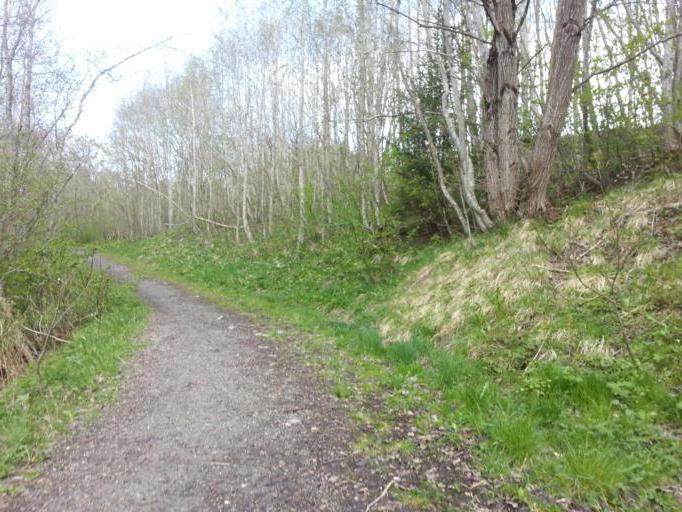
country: NO
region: Sor-Trondelag
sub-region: Trondheim
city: Trondheim
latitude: 63.3912
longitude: 10.3582
